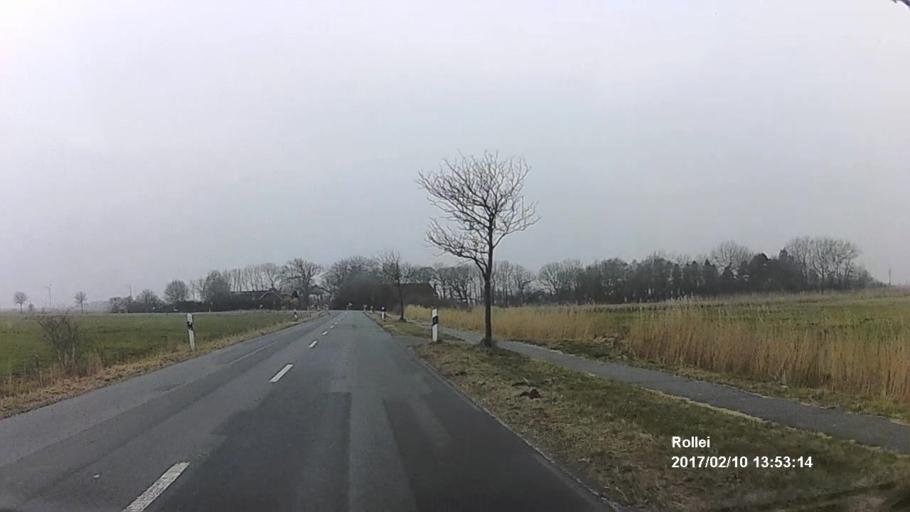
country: DE
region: Lower Saxony
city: Norddeich
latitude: 53.5754
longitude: 7.1364
